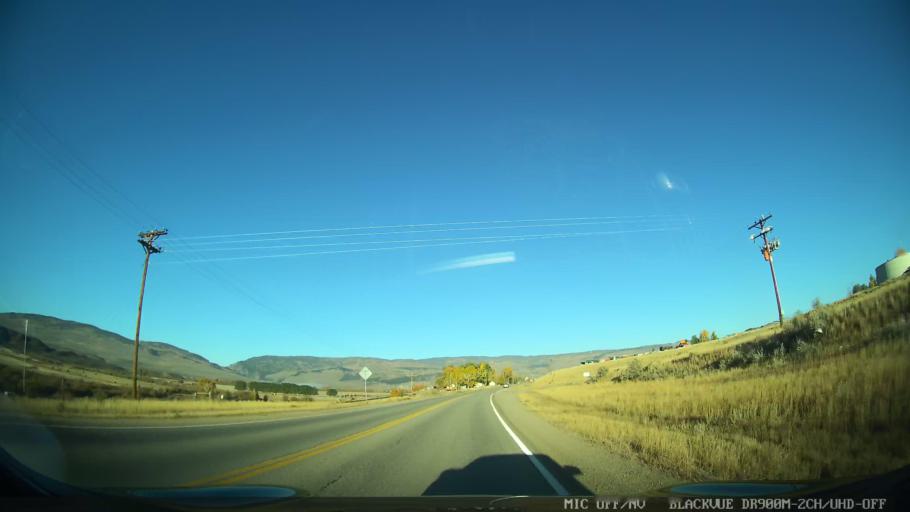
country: US
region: Colorado
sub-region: Grand County
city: Kremmling
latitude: 40.0519
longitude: -106.3766
